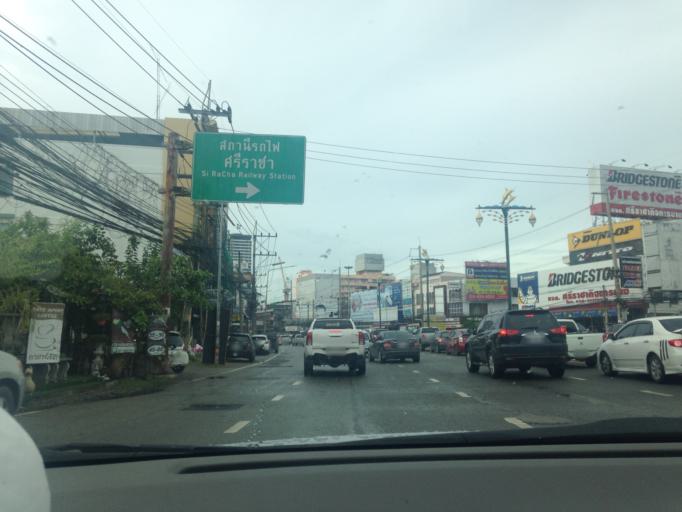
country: TH
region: Chon Buri
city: Si Racha
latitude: 13.1646
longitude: 100.9308
